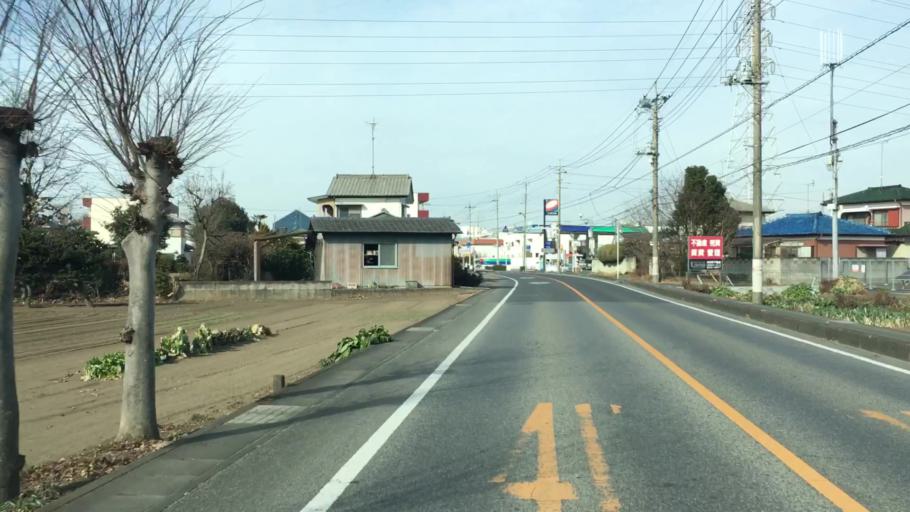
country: JP
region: Saitama
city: Menuma
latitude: 36.2501
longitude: 139.4296
